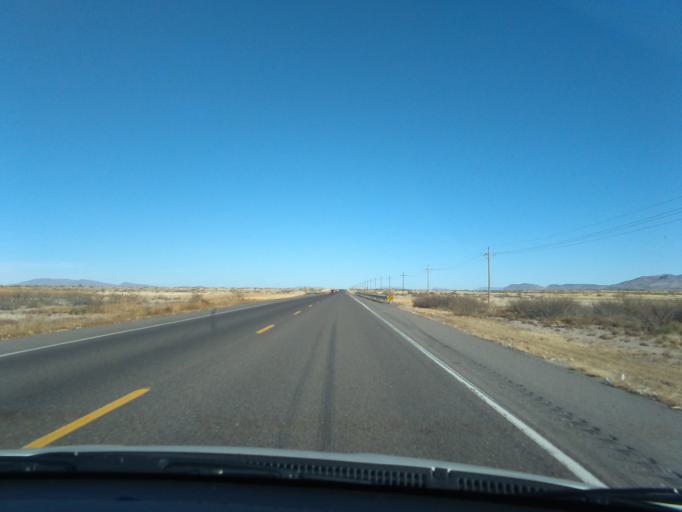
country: US
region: New Mexico
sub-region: Dona Ana County
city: Hatch
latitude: 32.5914
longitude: -107.3537
